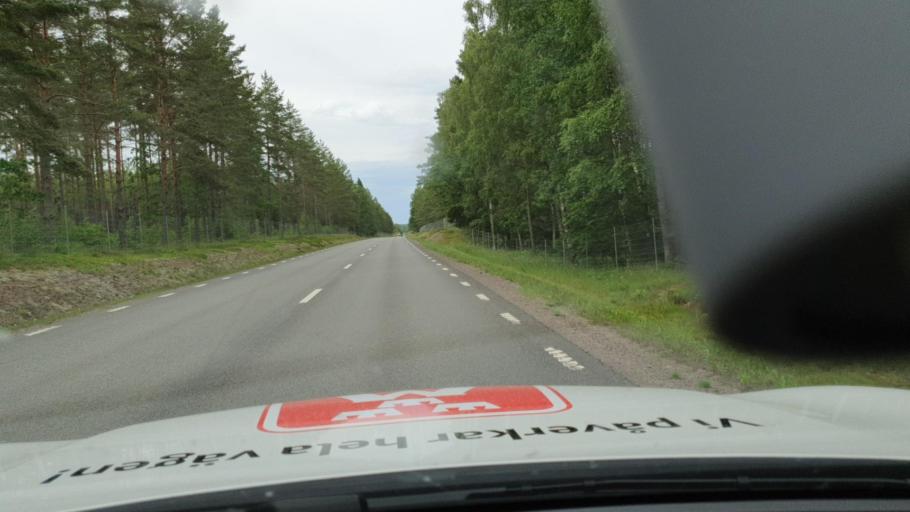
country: SE
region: Vaestra Goetaland
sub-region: Hjo Kommun
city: Hjo
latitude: 58.3727
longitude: 14.3517
